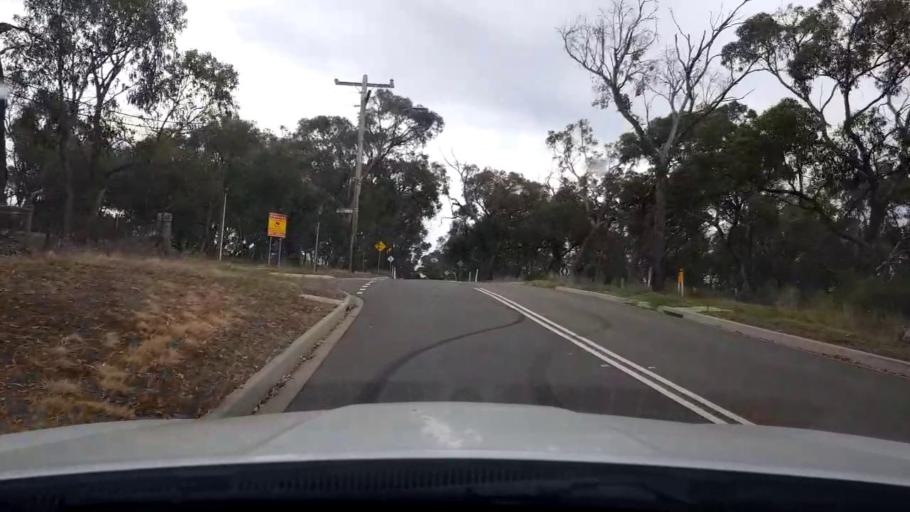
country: AU
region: Victoria
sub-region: Whittlesea
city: Whittlesea
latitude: -37.4912
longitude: 145.0470
